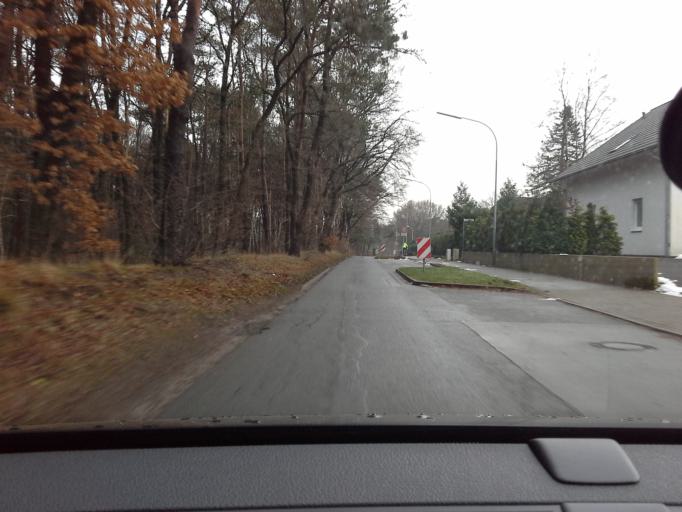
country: DE
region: Schleswig-Holstein
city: Henstedt-Ulzburg
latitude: 53.7481
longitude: 10.0125
